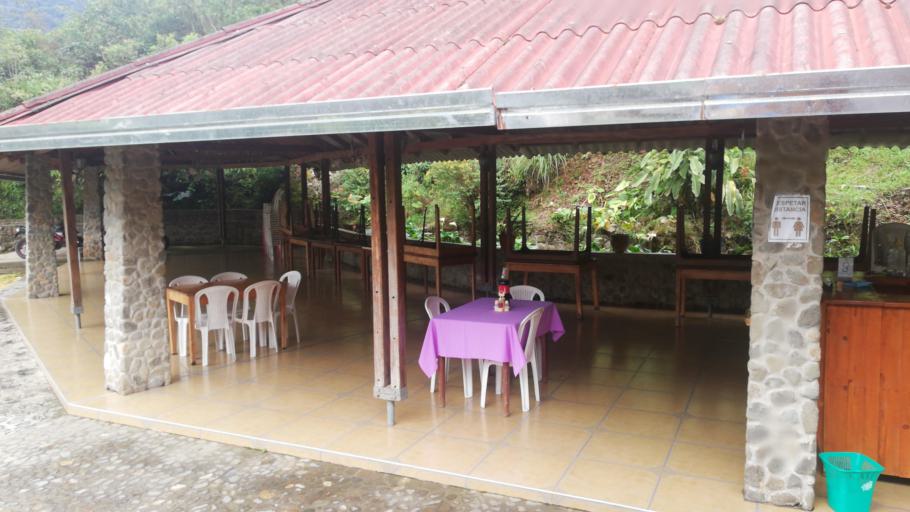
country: BO
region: Cochabamba
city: Colomi
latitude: -17.2144
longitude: -65.8267
